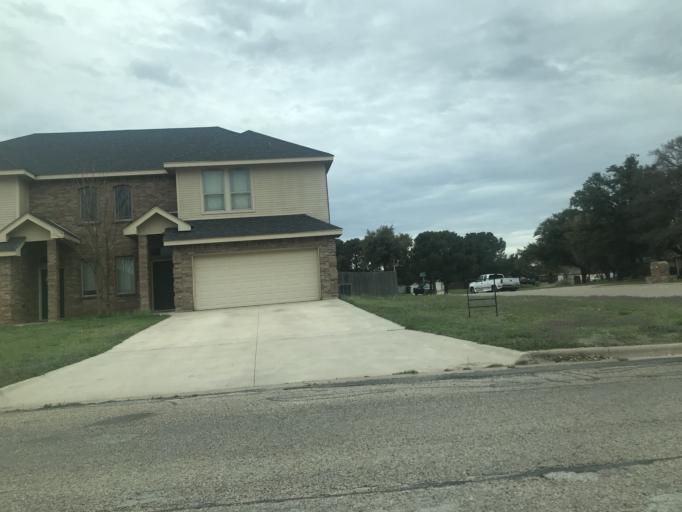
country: US
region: Texas
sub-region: Taylor County
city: Abilene
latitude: 32.4880
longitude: -99.6848
